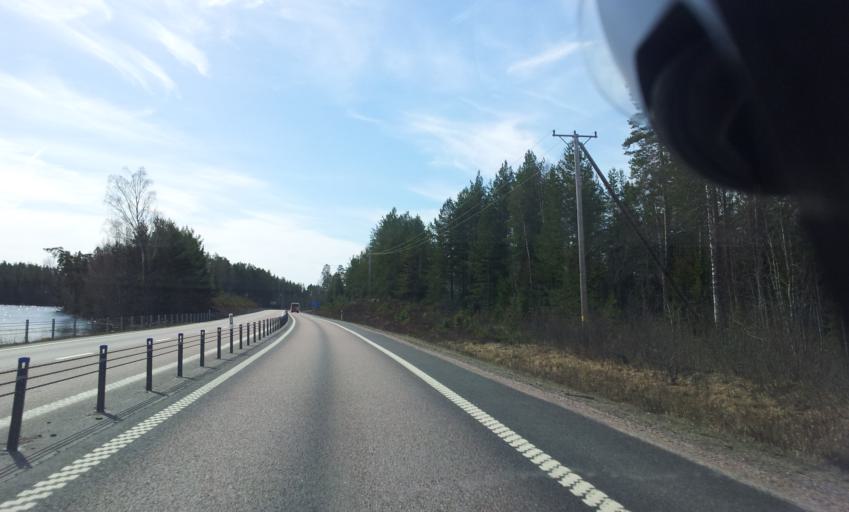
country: SE
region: Gaevleborg
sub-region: Soderhamns Kommun
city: Ljusne
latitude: 61.0853
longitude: 16.9733
